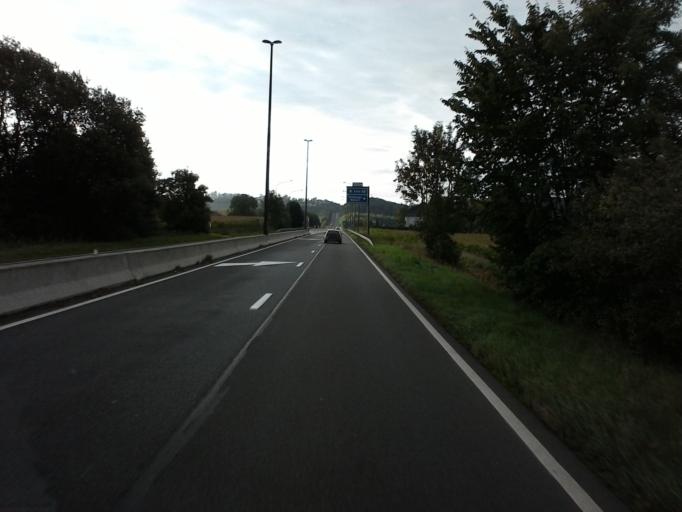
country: BE
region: Wallonia
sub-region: Province du Luxembourg
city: Attert
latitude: 49.7281
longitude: 5.7950
